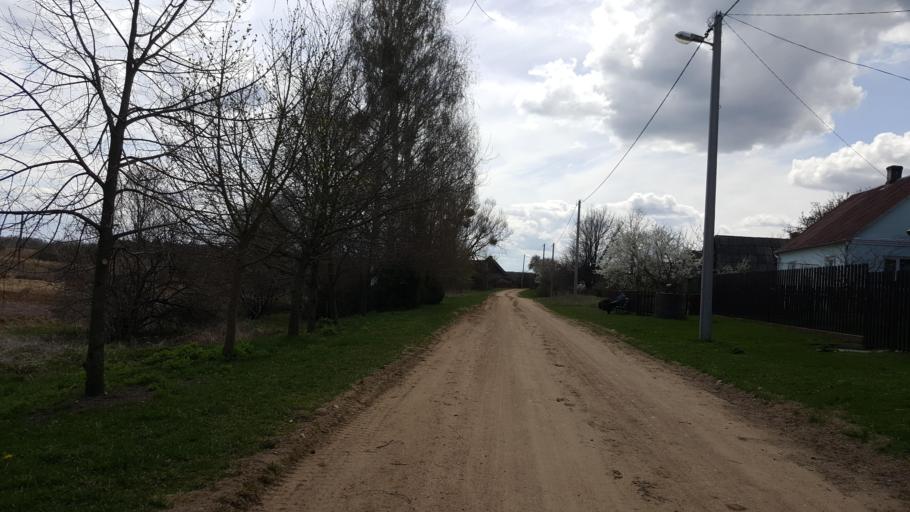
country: BY
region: Brest
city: Kamyanyets
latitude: 52.3524
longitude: 23.7323
